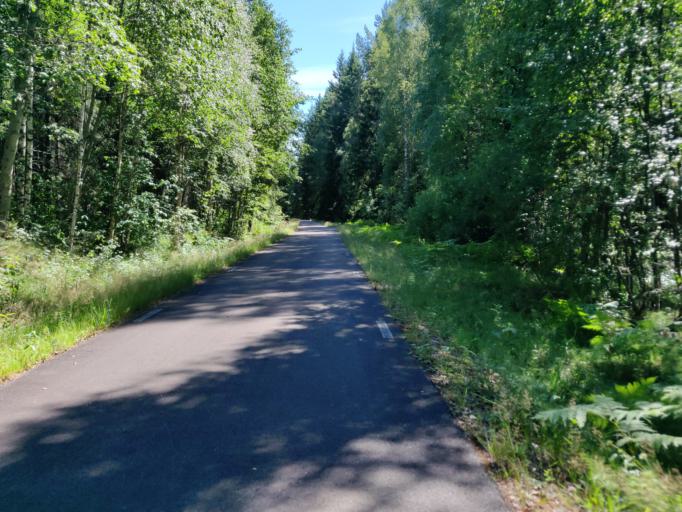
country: SE
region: Vaermland
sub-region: Hagfors Kommun
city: Hagfors
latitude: 59.9563
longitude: 13.5738
